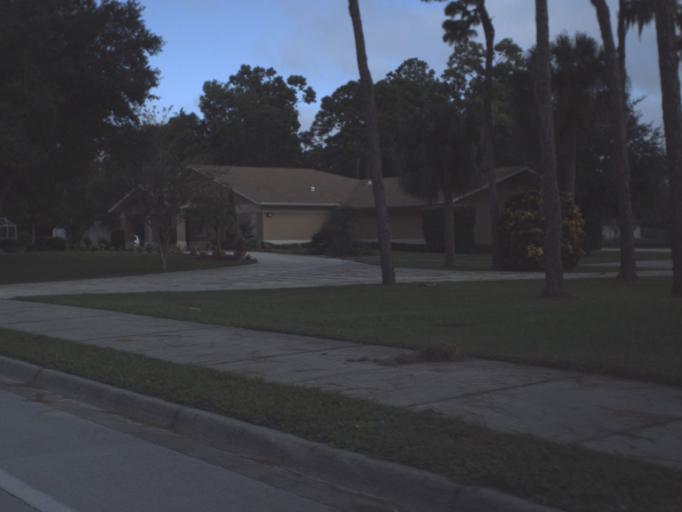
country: US
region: Florida
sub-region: Sarasota County
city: South Venice
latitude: 27.0189
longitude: -82.3882
